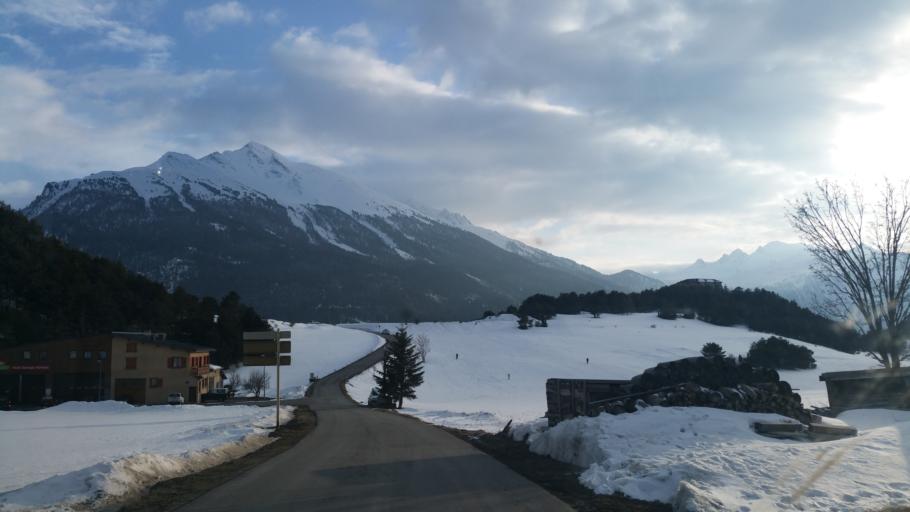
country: FR
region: Rhone-Alpes
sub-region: Departement de la Savoie
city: Modane
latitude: 45.2252
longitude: 6.7413
